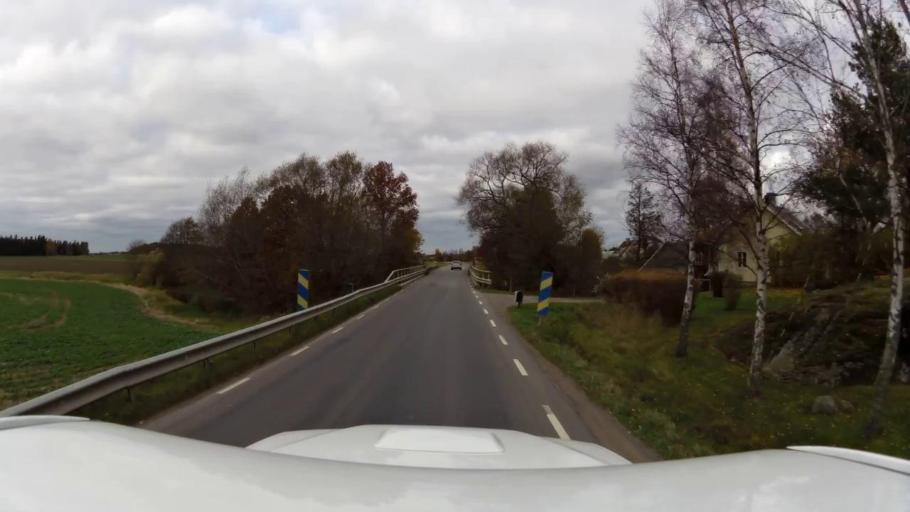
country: SE
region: OEstergoetland
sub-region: Linkopings Kommun
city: Linghem
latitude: 58.4205
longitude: 15.7320
